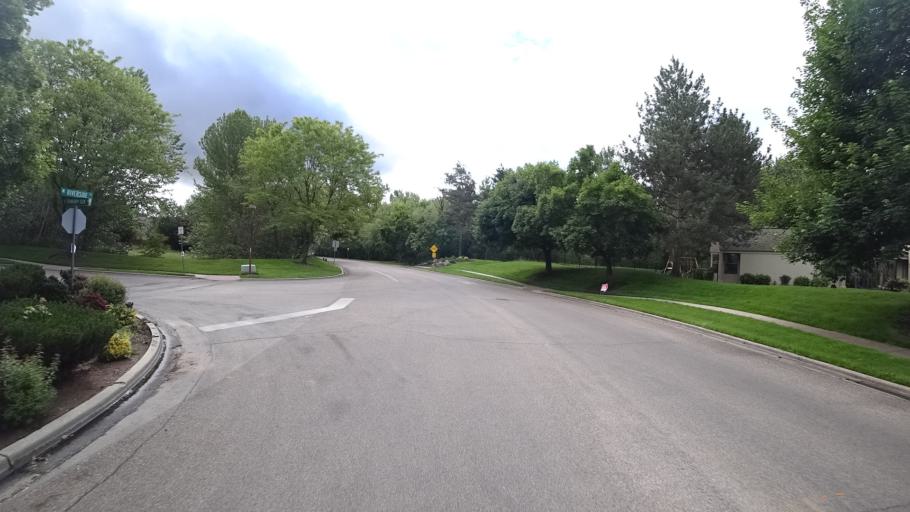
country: US
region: Idaho
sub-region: Ada County
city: Garden City
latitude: 43.6636
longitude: -116.2841
